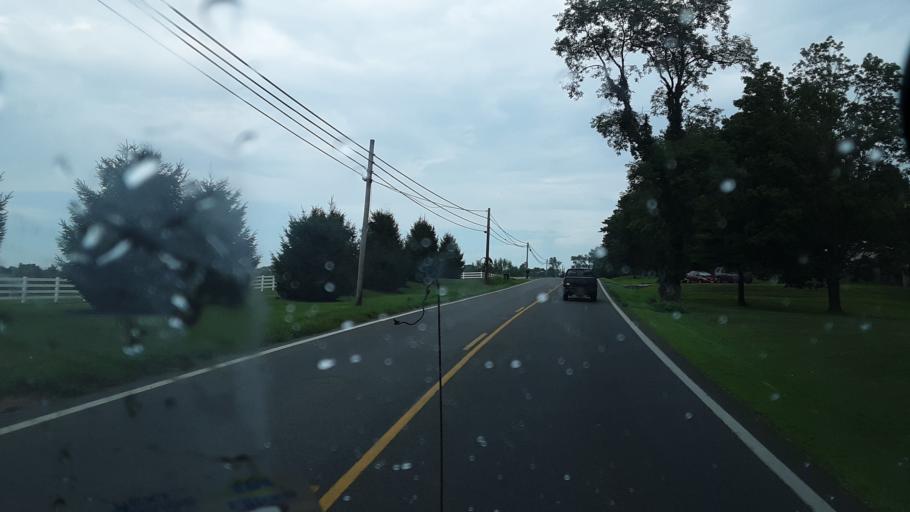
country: US
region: Ohio
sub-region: Fairfield County
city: Lancaster
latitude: 39.7549
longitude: -82.5821
